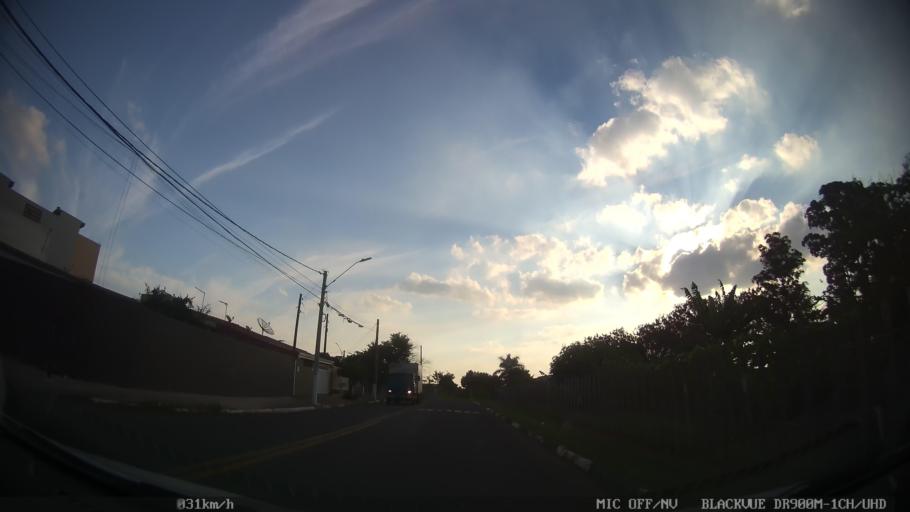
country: BR
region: Sao Paulo
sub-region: Hortolandia
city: Hortolandia
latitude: -22.8583
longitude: -47.1783
